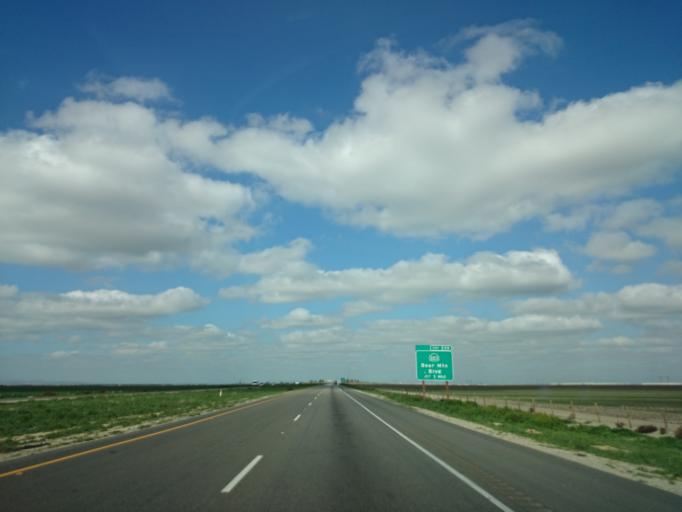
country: US
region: California
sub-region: Kern County
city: Greenfield
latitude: 35.1950
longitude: -119.1475
